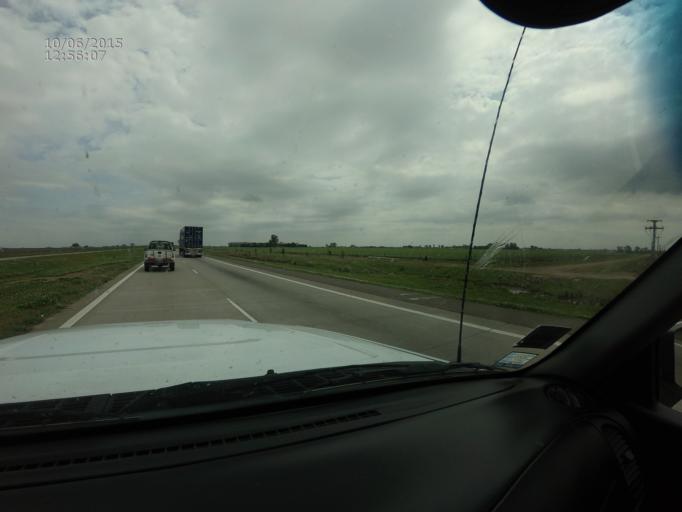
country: AR
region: Santa Fe
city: Armstrong
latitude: -32.8090
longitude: -61.6091
